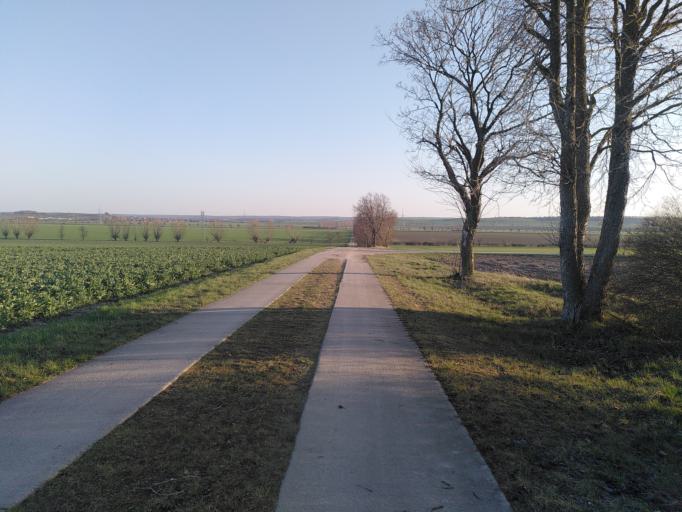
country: DE
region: Saxony-Anhalt
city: Ditfurt
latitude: 51.7952
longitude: 11.2297
